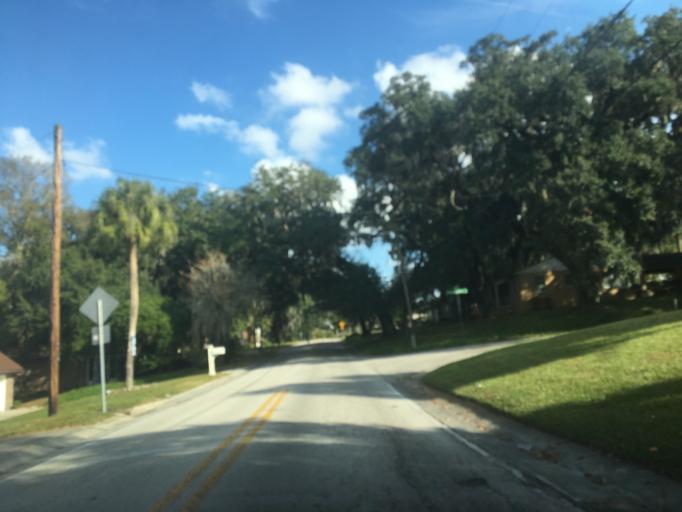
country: US
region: Florida
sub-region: Hillsborough County
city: Temple Terrace
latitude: 28.0089
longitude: -82.4176
